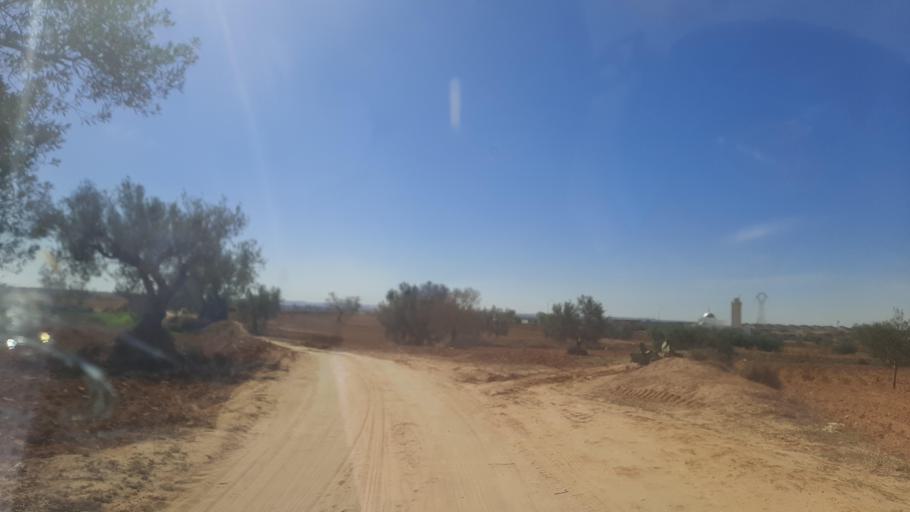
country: TN
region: Safaqis
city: Sfax
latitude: 34.7912
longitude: 10.5316
